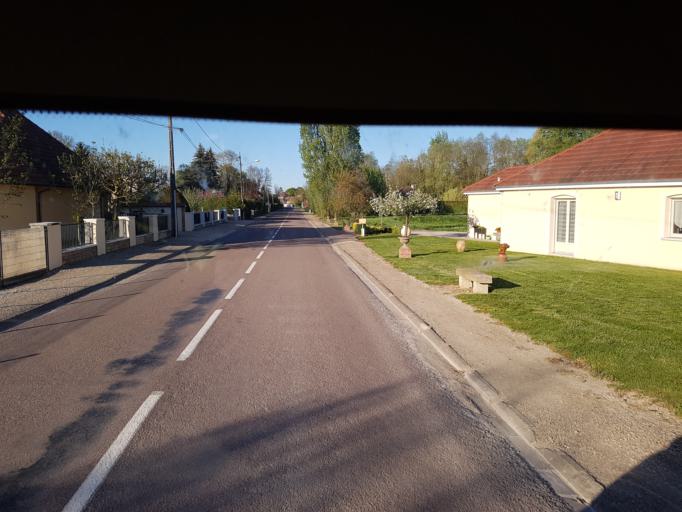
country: FR
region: Champagne-Ardenne
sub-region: Departement de l'Aube
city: Marigny-le-Chatel
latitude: 48.4370
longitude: 3.6767
